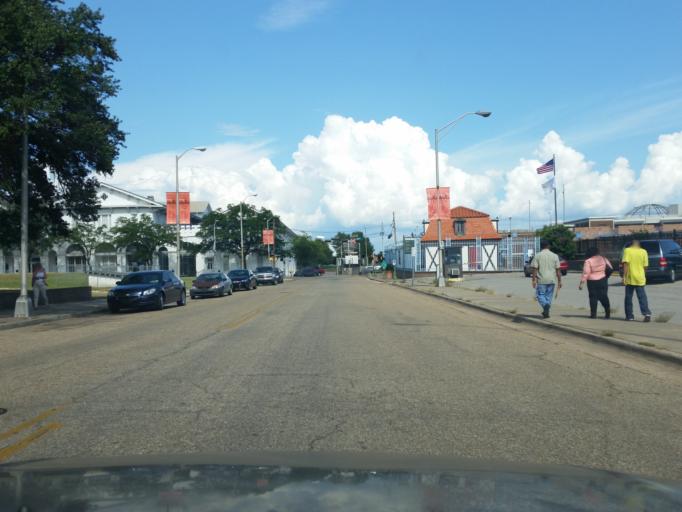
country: US
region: Alabama
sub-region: Mobile County
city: Mobile
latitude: 30.6888
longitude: -88.0409
